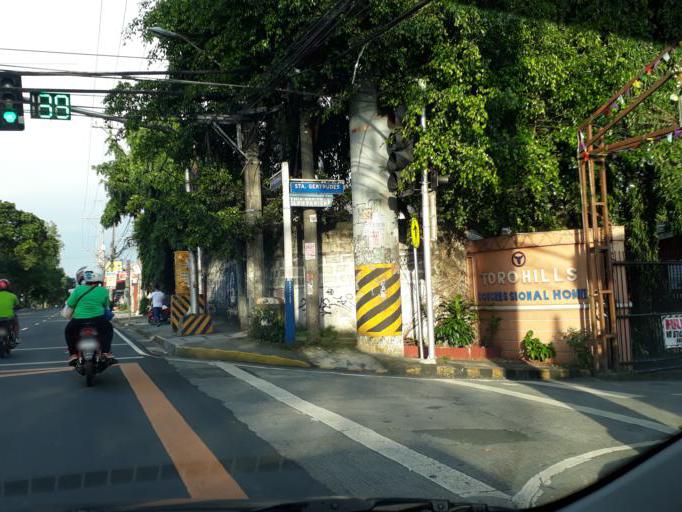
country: PH
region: Calabarzon
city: Bagong Pagasa
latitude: 14.6646
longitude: 121.0263
